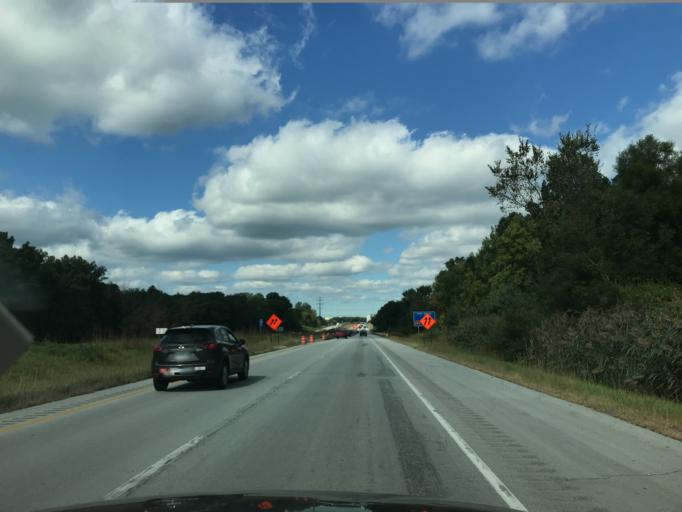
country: US
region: Ohio
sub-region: Cuyahoga County
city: Oakwood
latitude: 41.3445
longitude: -81.4992
